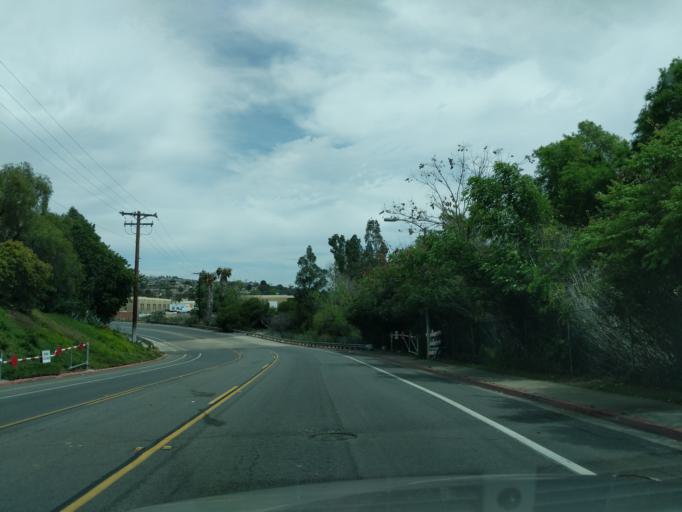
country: US
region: California
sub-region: San Diego County
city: La Mesa
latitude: 32.7837
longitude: -117.1052
